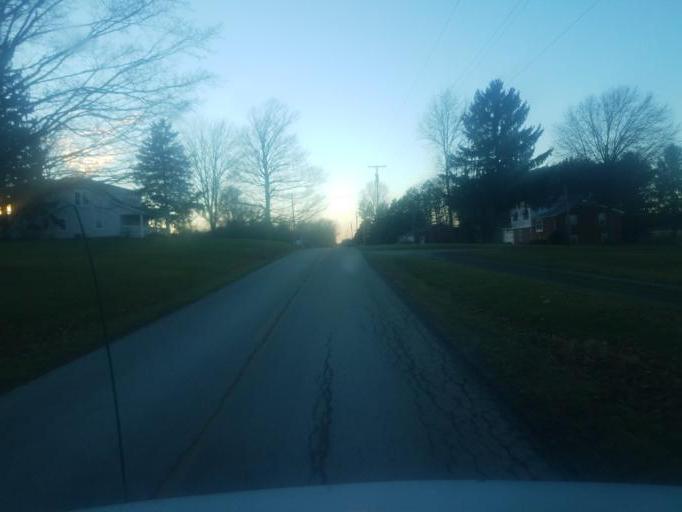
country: US
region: Ohio
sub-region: Richland County
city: Shelby
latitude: 40.8430
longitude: -82.5881
